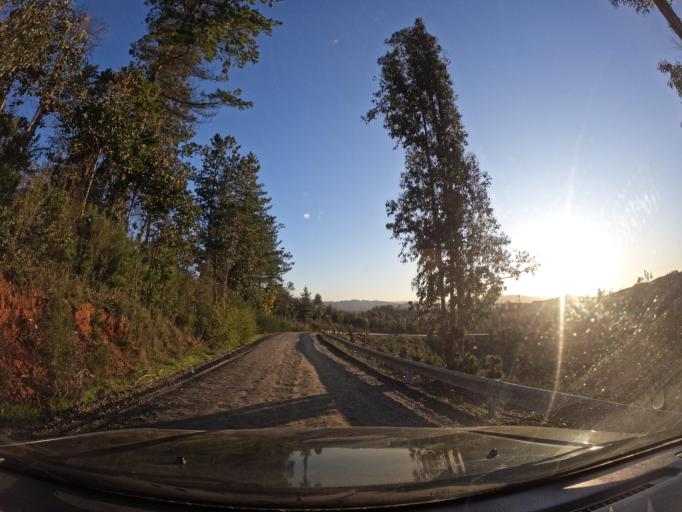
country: CL
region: Biobio
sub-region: Provincia de Concepcion
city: Chiguayante
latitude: -37.0097
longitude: -72.8908
